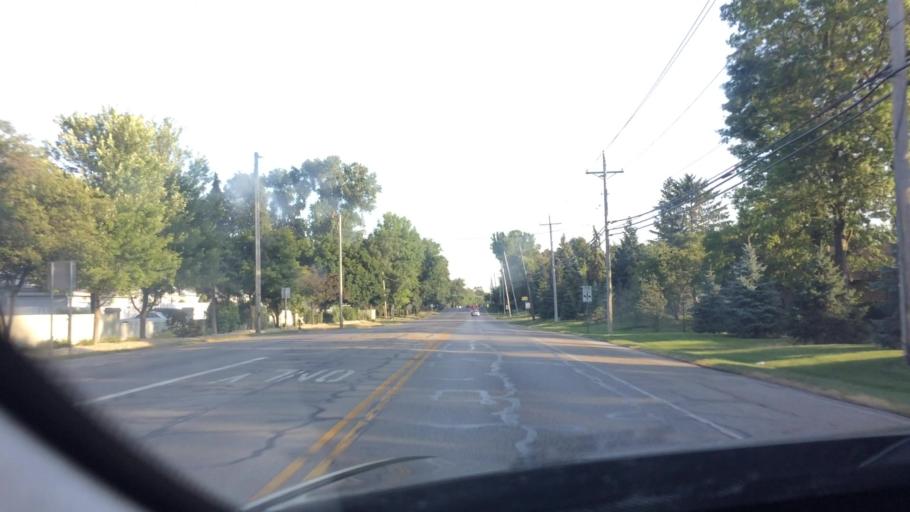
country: US
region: Ohio
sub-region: Lucas County
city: Holland
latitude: 41.6647
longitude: -83.7025
